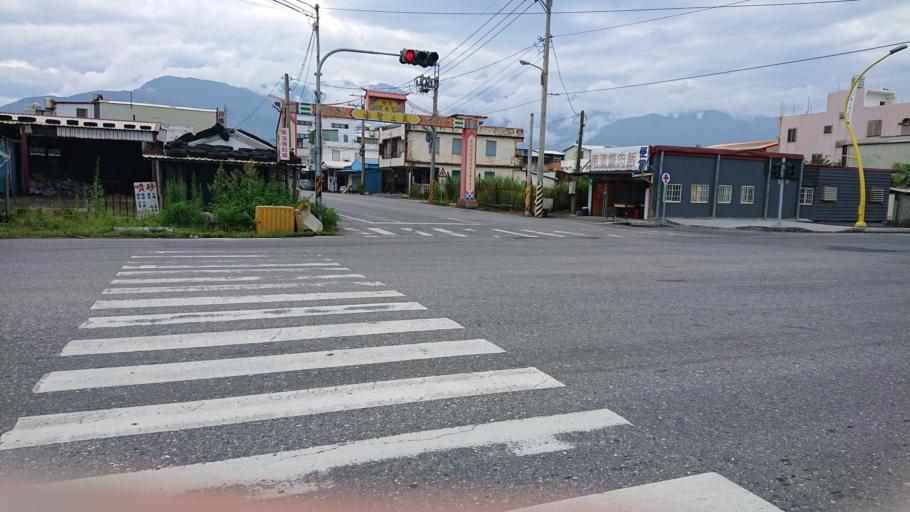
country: TW
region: Taiwan
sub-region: Hualien
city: Hualian
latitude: 23.9495
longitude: 121.5988
